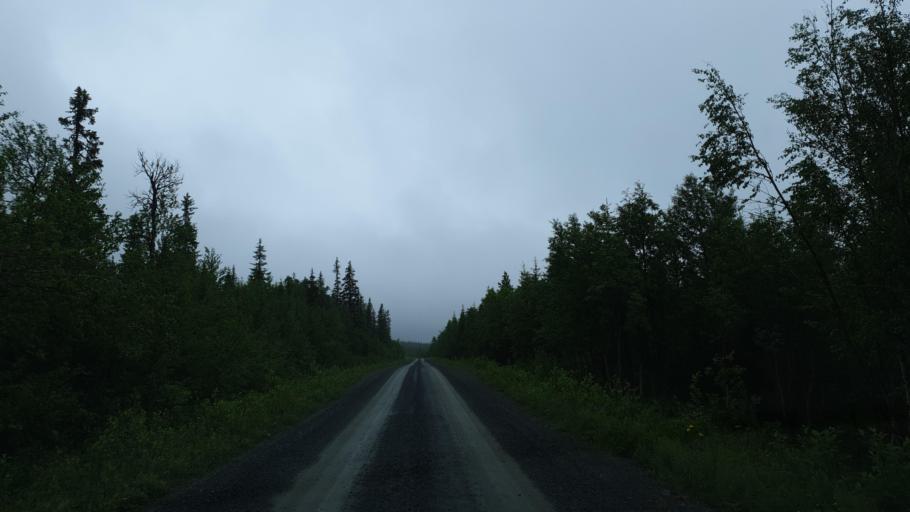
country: SE
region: Vaesterbotten
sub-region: Vilhelmina Kommun
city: Sjoberg
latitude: 65.3255
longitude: 15.9280
